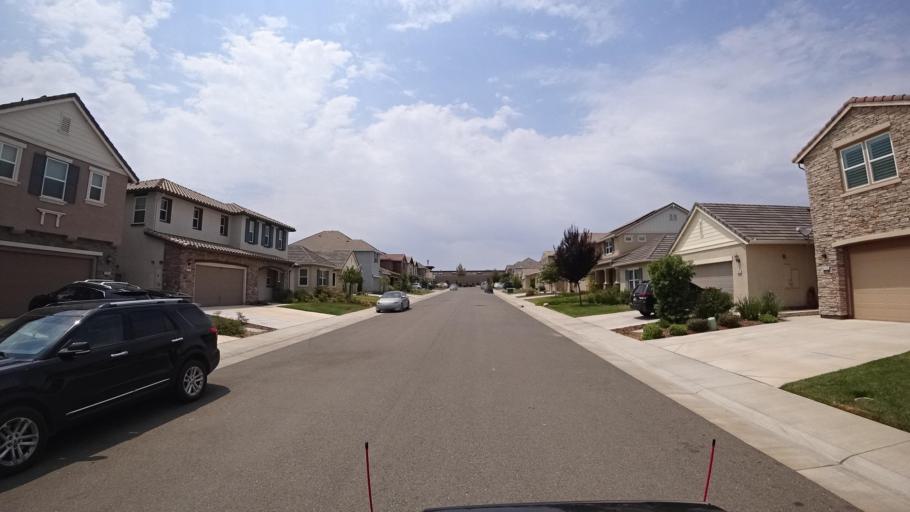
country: US
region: California
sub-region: Placer County
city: Loomis
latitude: 38.8022
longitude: -121.1990
